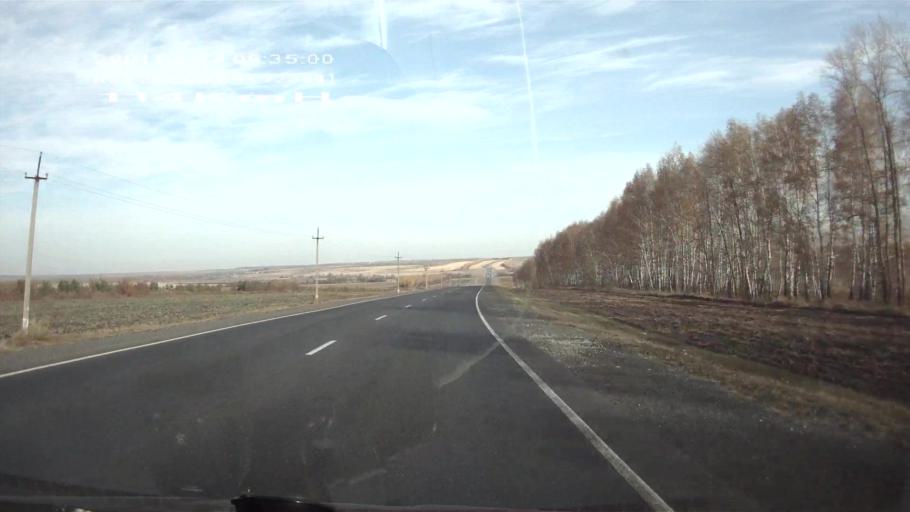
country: RU
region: Penza
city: Mokshan
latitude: 53.5967
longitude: 44.7240
